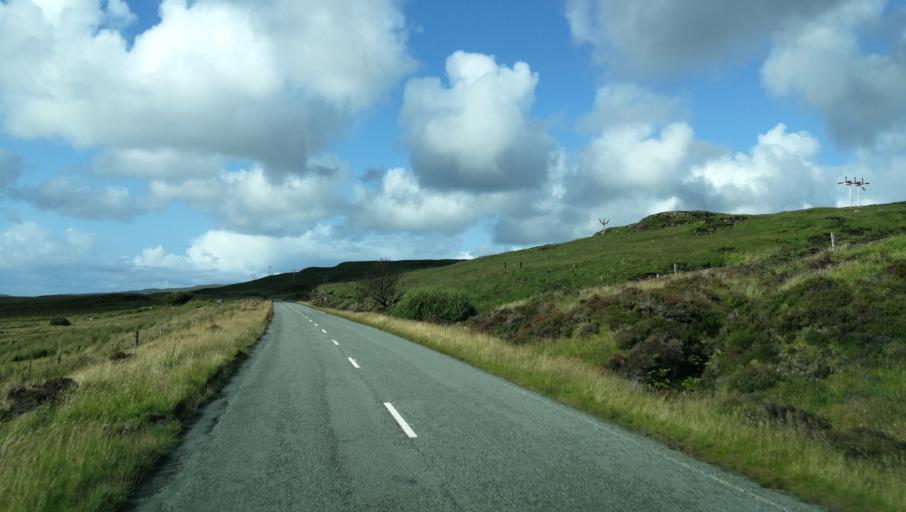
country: GB
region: Scotland
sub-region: Highland
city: Isle of Skye
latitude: 57.4556
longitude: -6.5423
